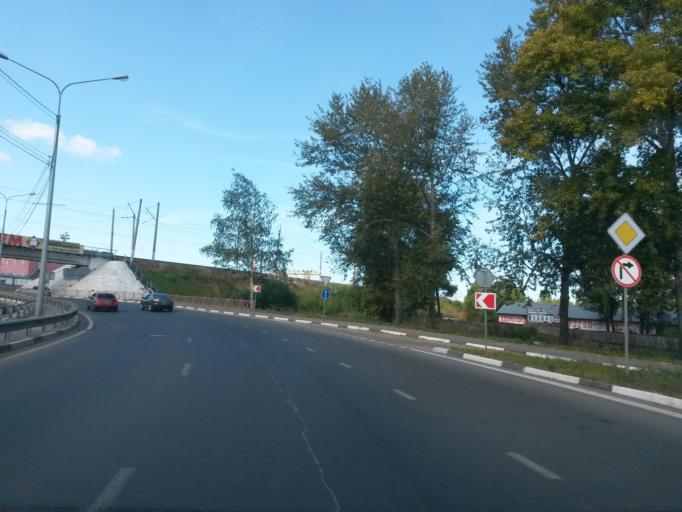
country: RU
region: Jaroslavl
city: Yaroslavl
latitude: 57.5975
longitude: 39.8937
